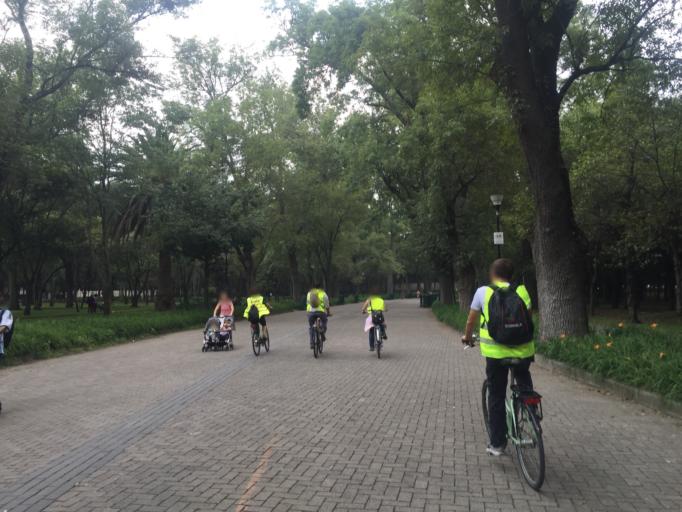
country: MX
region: Mexico City
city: Polanco
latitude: 19.4192
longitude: -99.1906
